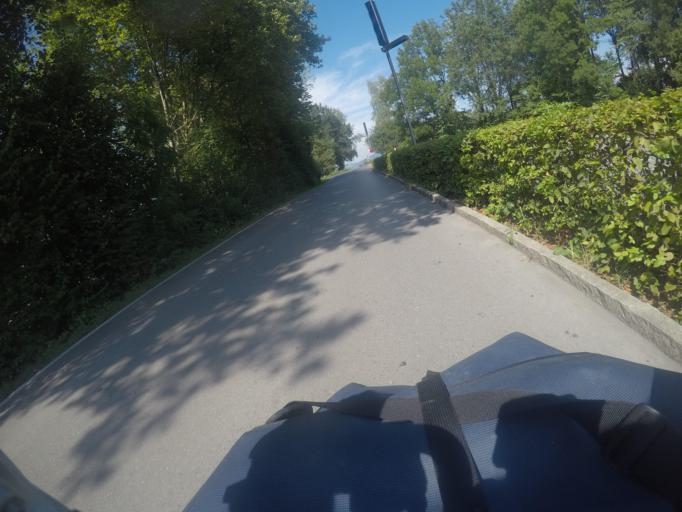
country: AT
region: Vorarlberg
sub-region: Politischer Bezirk Bregenz
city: Hard
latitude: 47.4458
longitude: 9.6964
